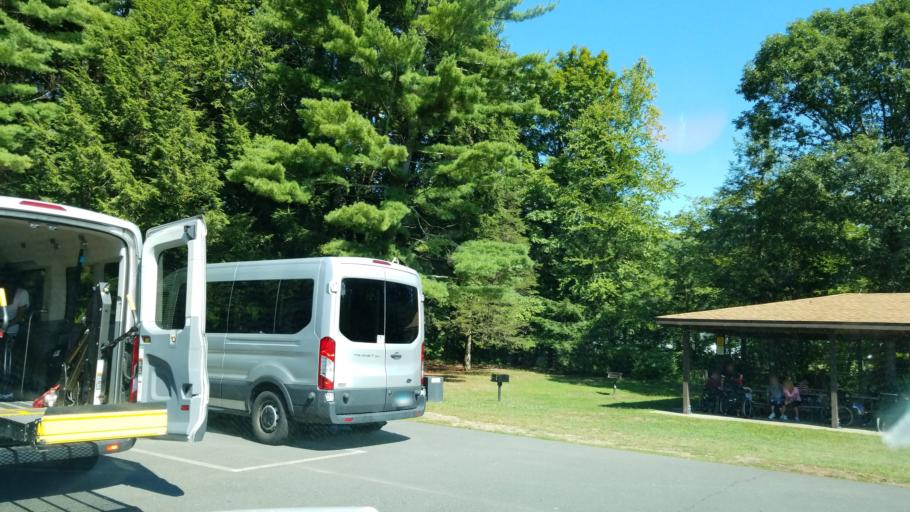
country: US
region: Connecticut
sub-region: Litchfield County
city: Thomaston
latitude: 41.6551
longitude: -73.0982
